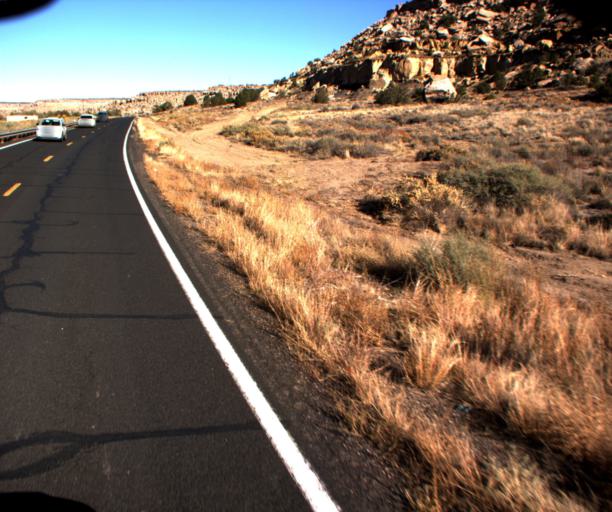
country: US
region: Arizona
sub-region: Navajo County
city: First Mesa
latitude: 35.8186
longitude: -110.2167
